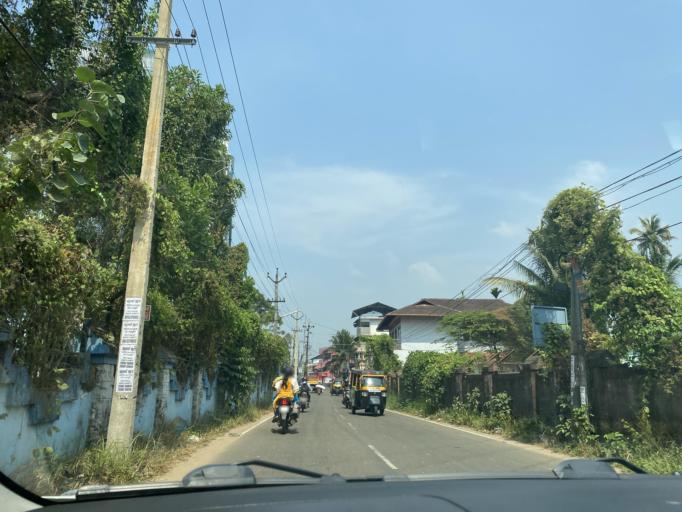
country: IN
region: Kerala
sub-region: Alappuzha
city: Arukutti
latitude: 9.9098
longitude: 76.3182
